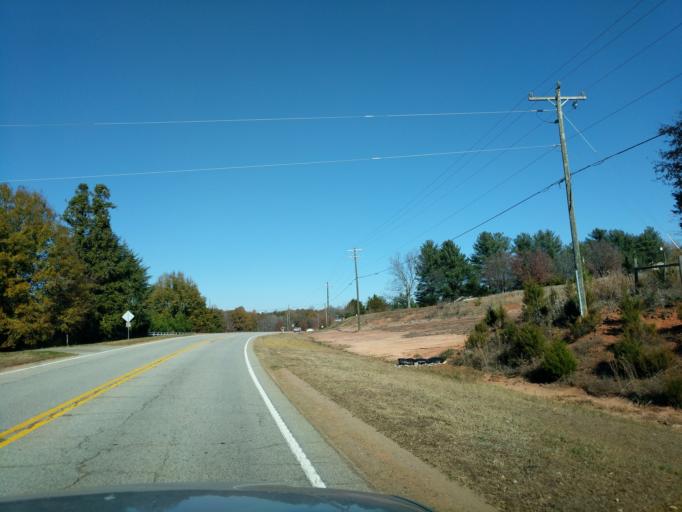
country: US
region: South Carolina
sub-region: Spartanburg County
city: Inman Mills
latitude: 35.0366
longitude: -82.1852
